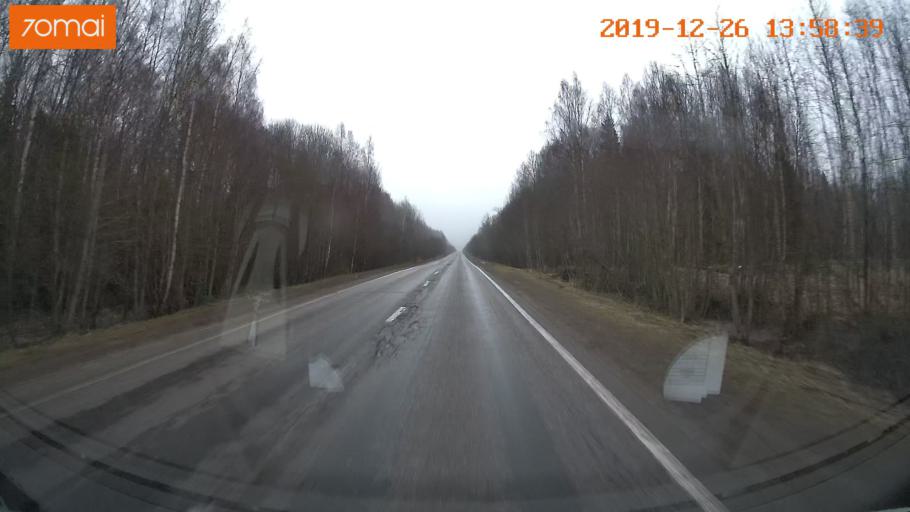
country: RU
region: Jaroslavl
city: Poshekhon'ye
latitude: 58.5723
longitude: 38.7057
